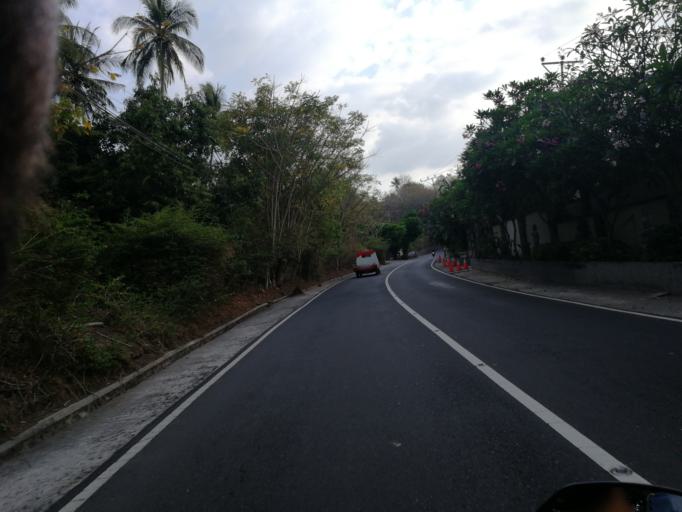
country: ID
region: West Nusa Tenggara
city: Karangsubagan
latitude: -8.4810
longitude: 116.0386
